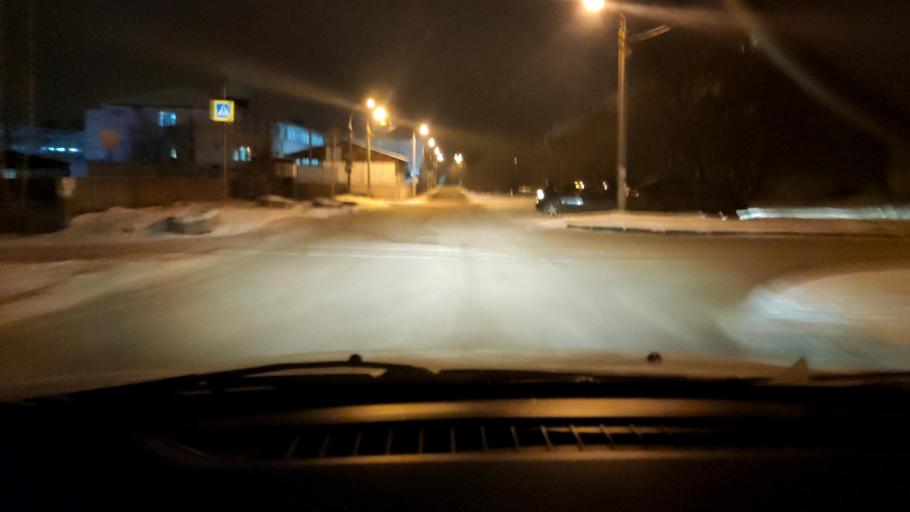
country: RU
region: Perm
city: Kondratovo
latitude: 58.0365
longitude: 56.0377
